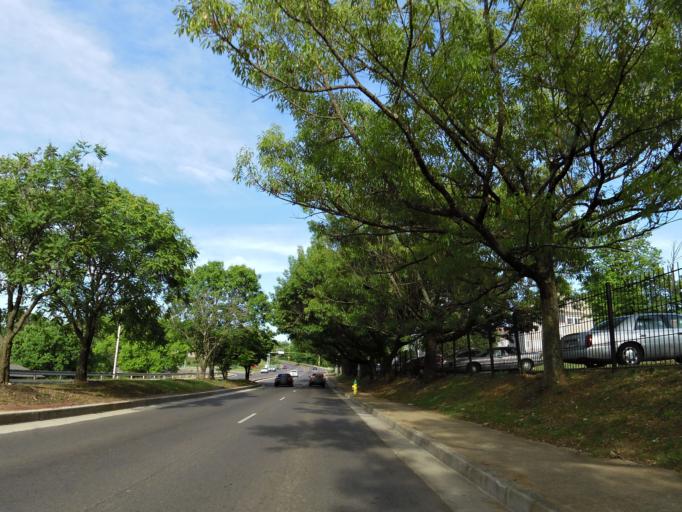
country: US
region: Tennessee
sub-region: Knox County
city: Knoxville
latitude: 35.9703
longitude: -83.9090
